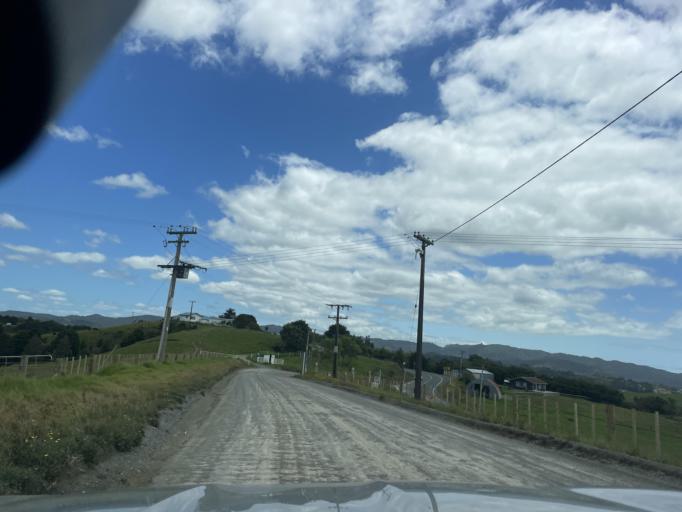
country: NZ
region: Auckland
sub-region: Auckland
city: Wellsford
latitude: -36.1342
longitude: 174.5361
